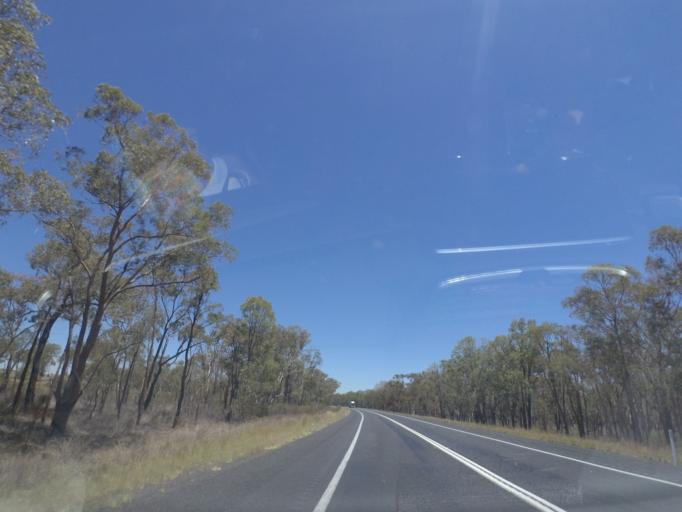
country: AU
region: New South Wales
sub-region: Warrumbungle Shire
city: Coonabarabran
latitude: -31.2076
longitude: 149.3325
